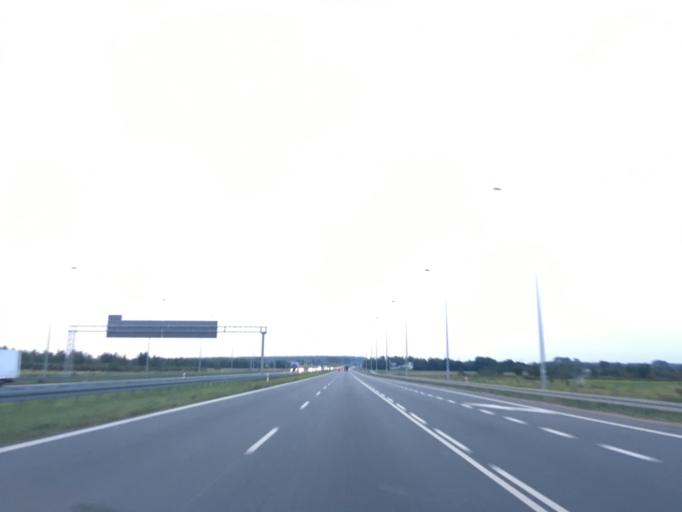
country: PL
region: Lodz Voivodeship
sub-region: Powiat zgierski
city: Strykow
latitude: 51.8820
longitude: 19.6436
